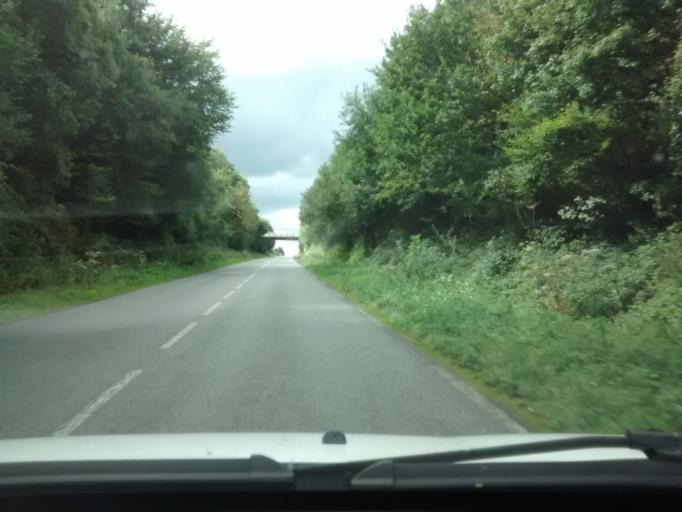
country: FR
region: Brittany
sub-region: Departement d'Ille-et-Vilaine
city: Miniac-Morvan
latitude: 48.5009
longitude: -1.9010
